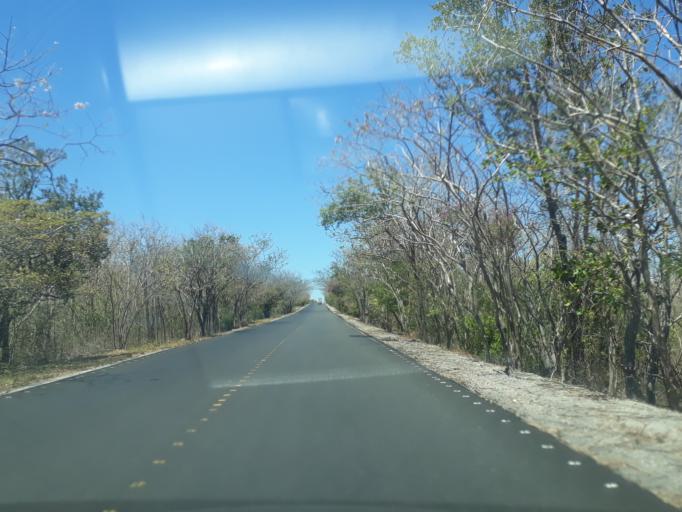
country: CR
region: Guanacaste
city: La Cruz
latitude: 10.9212
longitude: -85.6053
